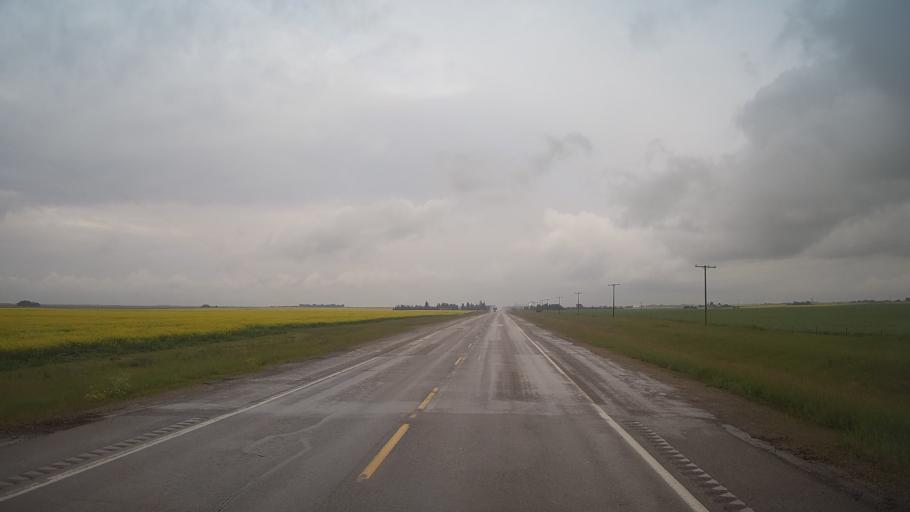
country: CA
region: Saskatchewan
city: Unity
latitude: 52.4349
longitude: -109.0147
